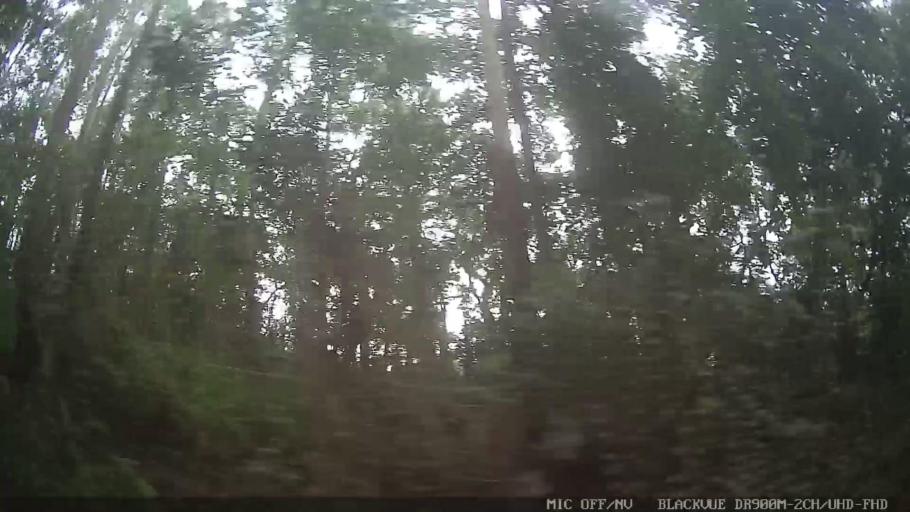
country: BR
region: Sao Paulo
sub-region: Suzano
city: Suzano
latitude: -23.6573
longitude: -46.2521
